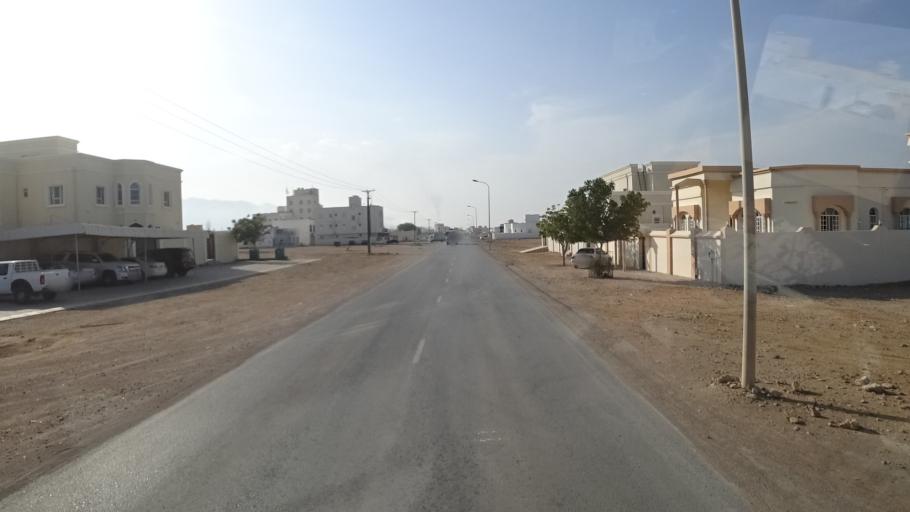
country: OM
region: Ash Sharqiyah
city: Sur
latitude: 22.6134
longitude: 59.4638
